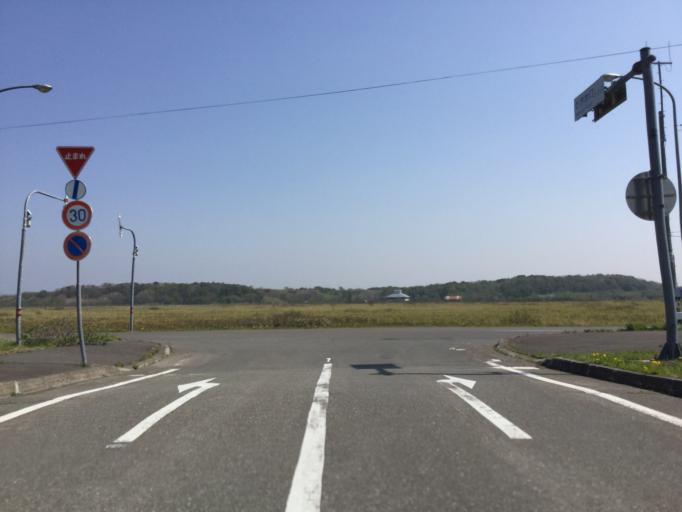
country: JP
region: Hokkaido
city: Makubetsu
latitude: 45.3989
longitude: 141.7996
